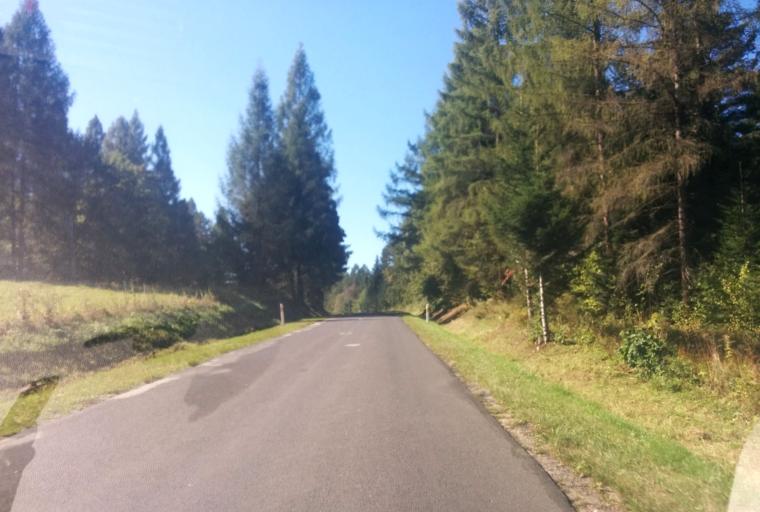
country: PL
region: Subcarpathian Voivodeship
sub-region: Powiat bieszczadzki
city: Czarna
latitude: 49.3160
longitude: 22.6494
